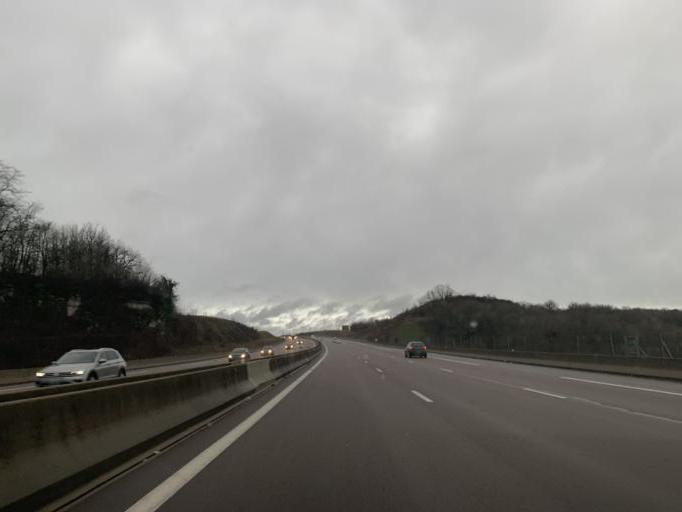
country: FR
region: Bourgogne
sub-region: Departement de la Cote-d'Or
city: Selongey
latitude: 47.7432
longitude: 5.1948
